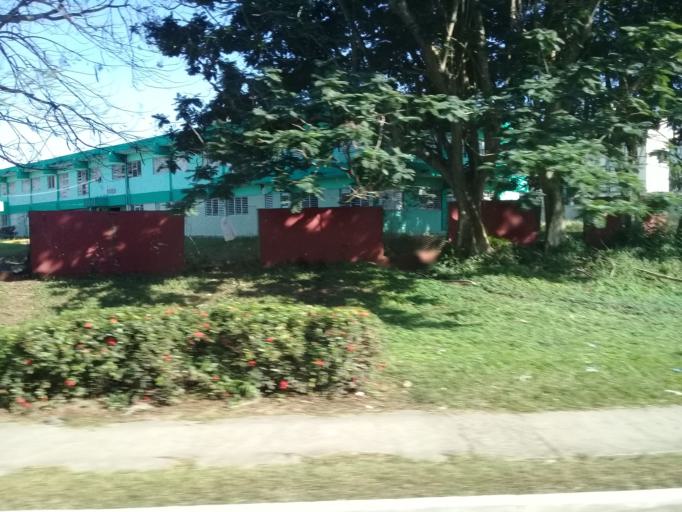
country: CU
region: Pinar del Rio
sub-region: Municipio de Pinar del Rio
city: Pinar del Rio
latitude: 22.4283
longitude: -83.6892
